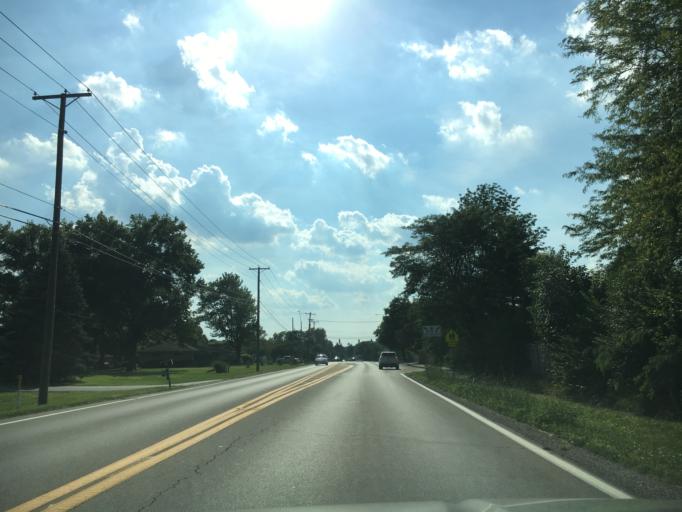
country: US
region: Ohio
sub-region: Franklin County
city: Lincoln Village
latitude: 39.9827
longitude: -83.1634
